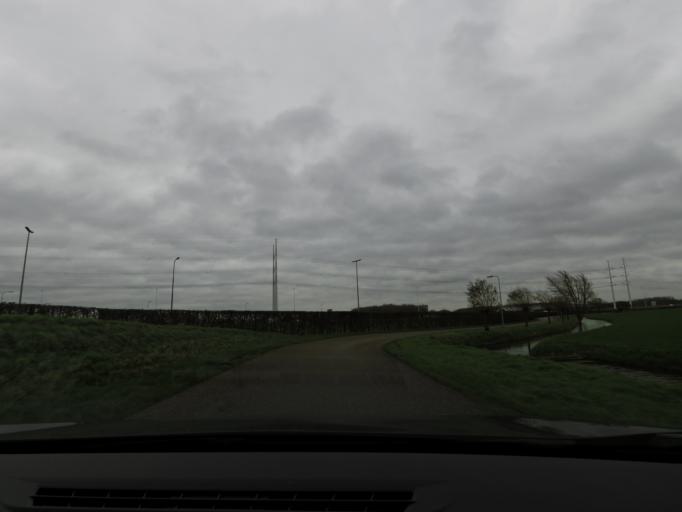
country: NL
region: South Holland
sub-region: Gemeente Delft
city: Delft
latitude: 51.9934
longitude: 4.3166
